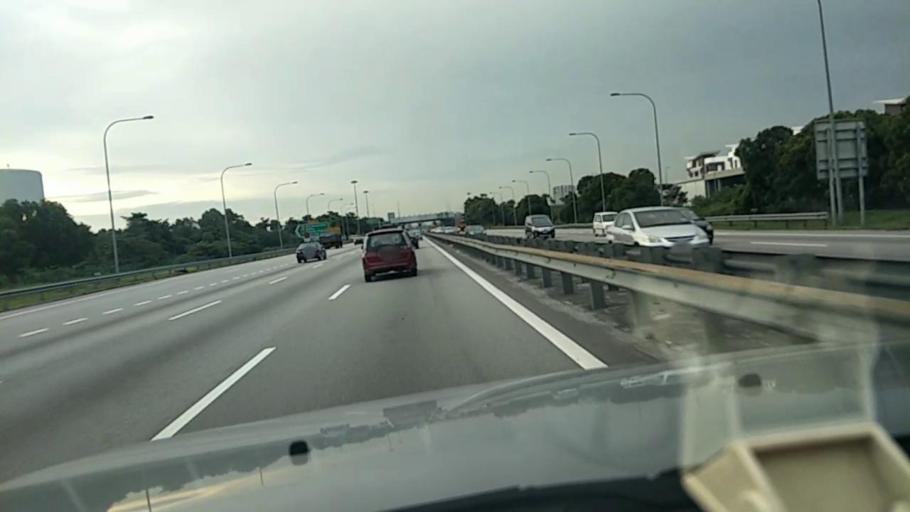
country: MY
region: Selangor
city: Subang Jaya
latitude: 2.9566
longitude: 101.5844
